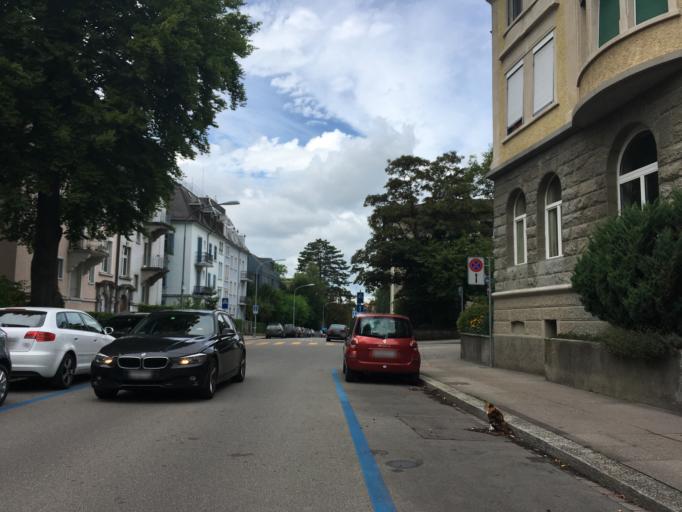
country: CH
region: Zurich
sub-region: Bezirk Zuerich
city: Zuerich (Kreis 6) / Oberstrass
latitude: 47.3816
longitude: 8.5510
